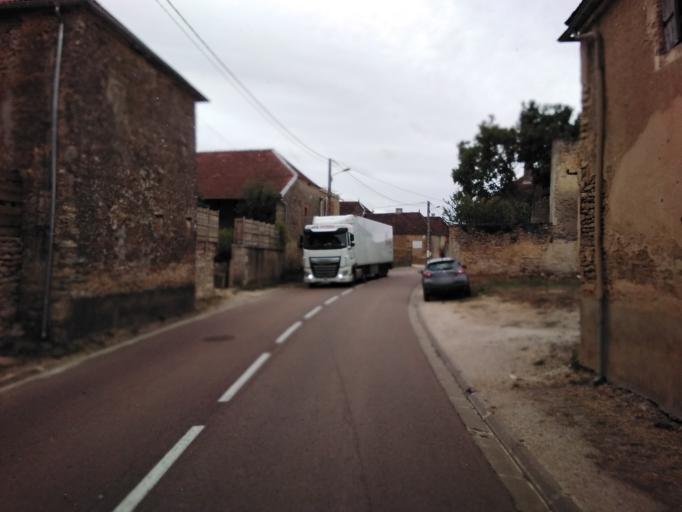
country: FR
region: Champagne-Ardenne
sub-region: Departement de l'Aube
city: Vendeuvre-sur-Barse
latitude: 48.1946
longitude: 4.4413
